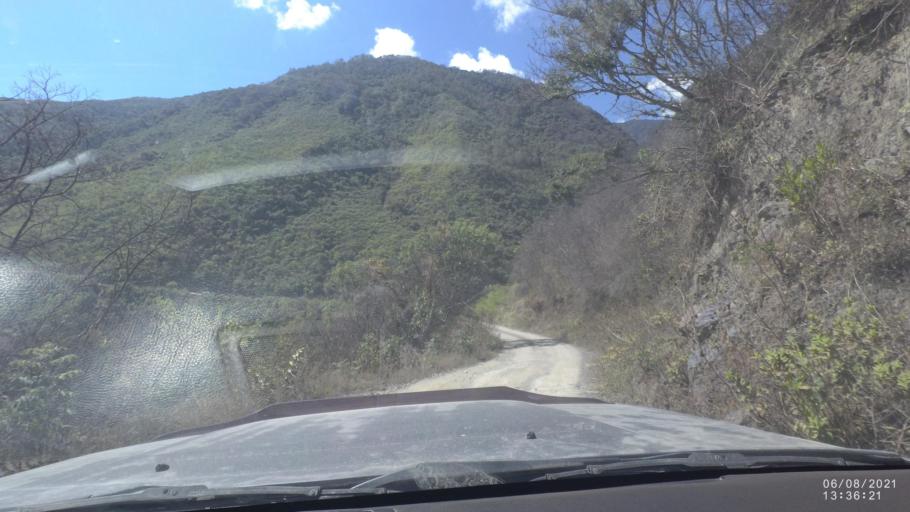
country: BO
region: La Paz
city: Quime
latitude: -16.6914
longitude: -66.7234
